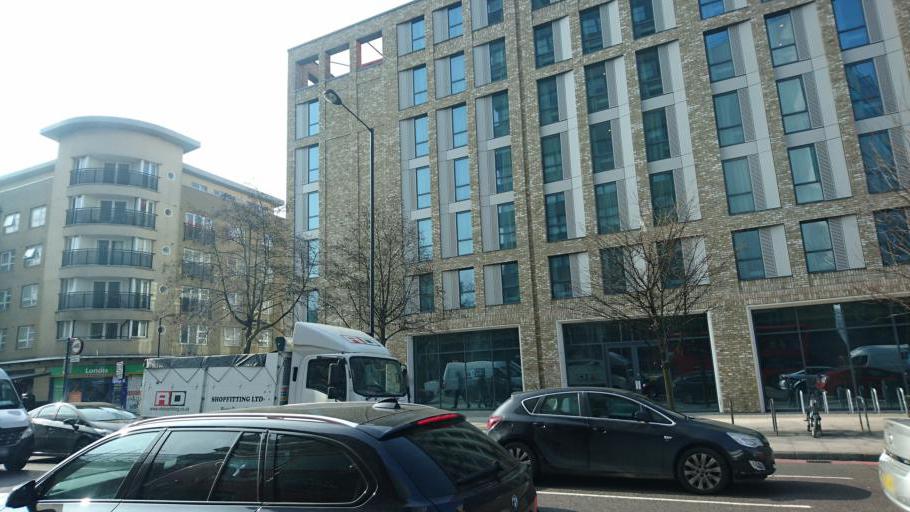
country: GB
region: England
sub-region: Greater London
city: Barnsbury
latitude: 51.5521
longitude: -0.1119
